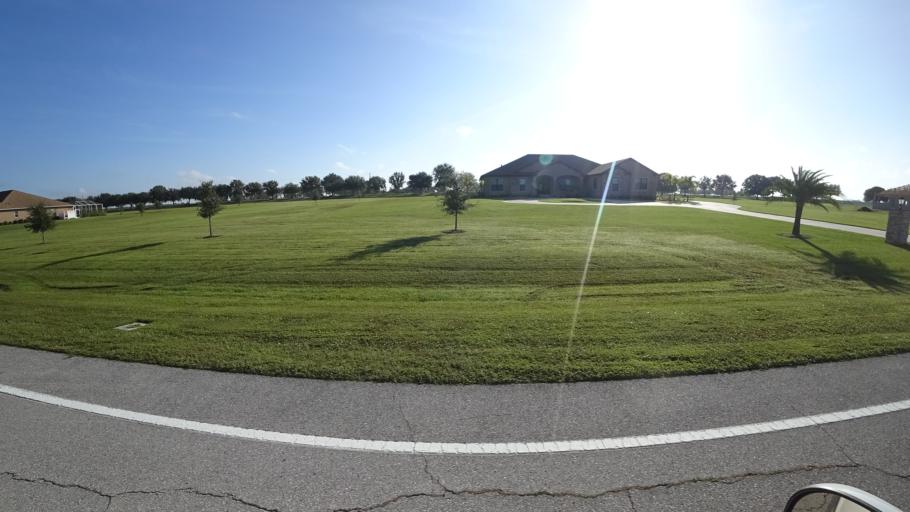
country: US
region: Florida
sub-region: Hillsborough County
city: Sun City Center
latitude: 27.5747
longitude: -82.3533
